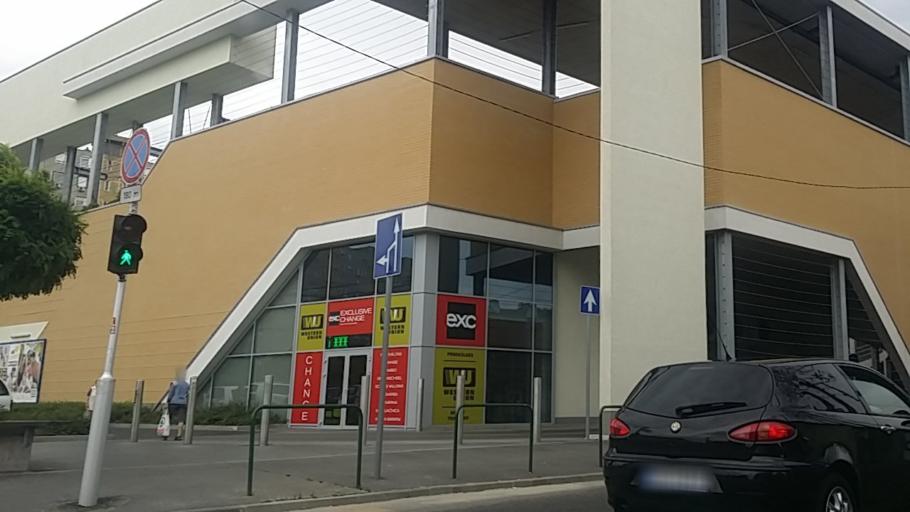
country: HU
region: Budapest
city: Budapest XIX. keruelet
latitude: 47.4574
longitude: 19.1449
